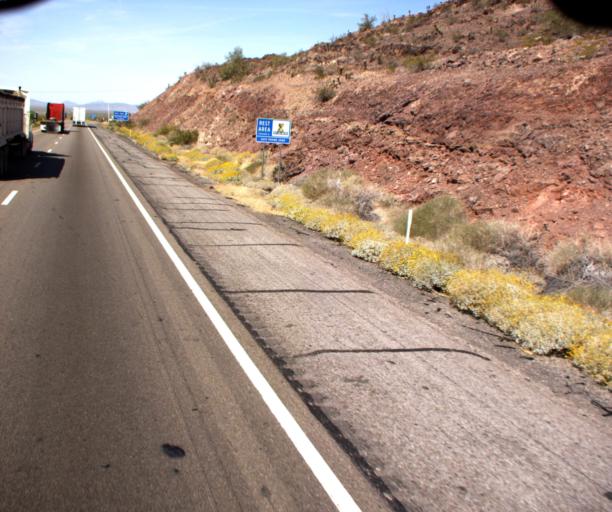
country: US
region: Arizona
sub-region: La Paz County
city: Salome
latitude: 33.6120
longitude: -113.6374
